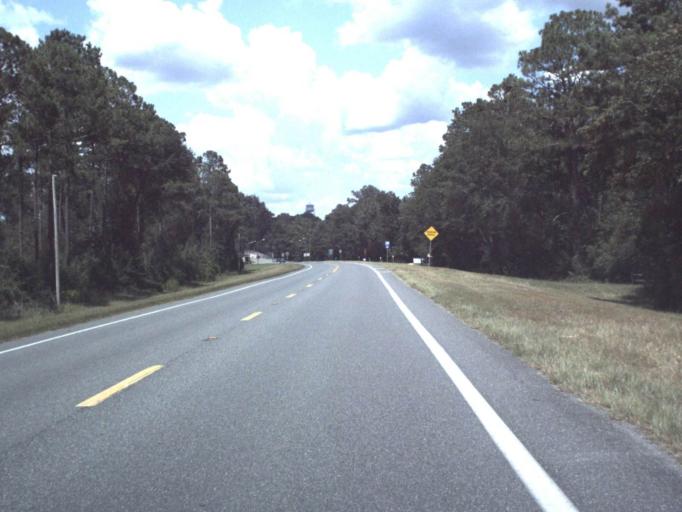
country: US
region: Florida
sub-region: Suwannee County
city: Wellborn
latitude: 30.3254
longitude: -82.7650
